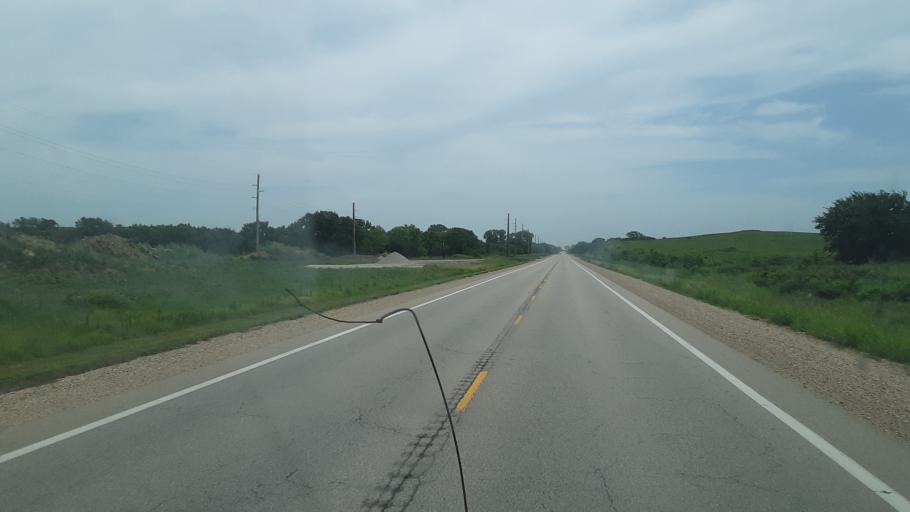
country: US
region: Kansas
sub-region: Woodson County
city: Yates Center
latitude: 37.8367
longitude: -95.9973
